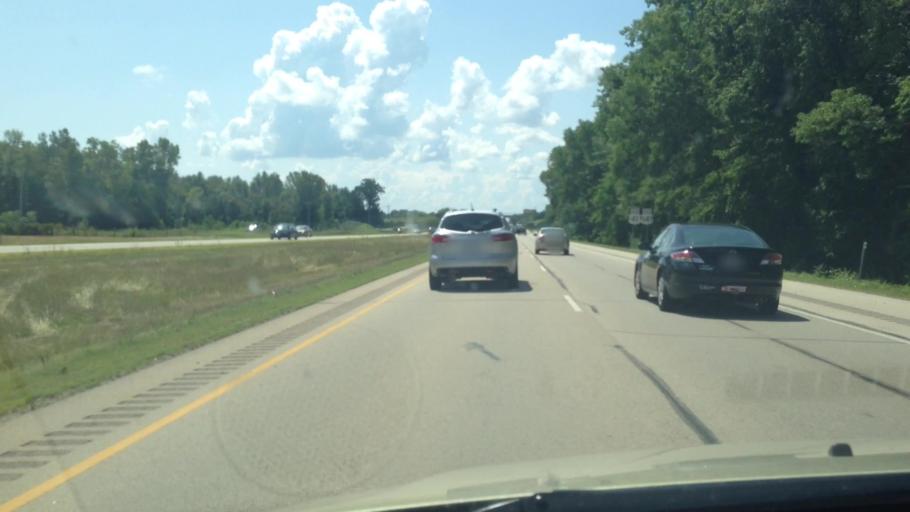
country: US
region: Wisconsin
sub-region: Brown County
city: Suamico
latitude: 44.7147
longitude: -88.0510
